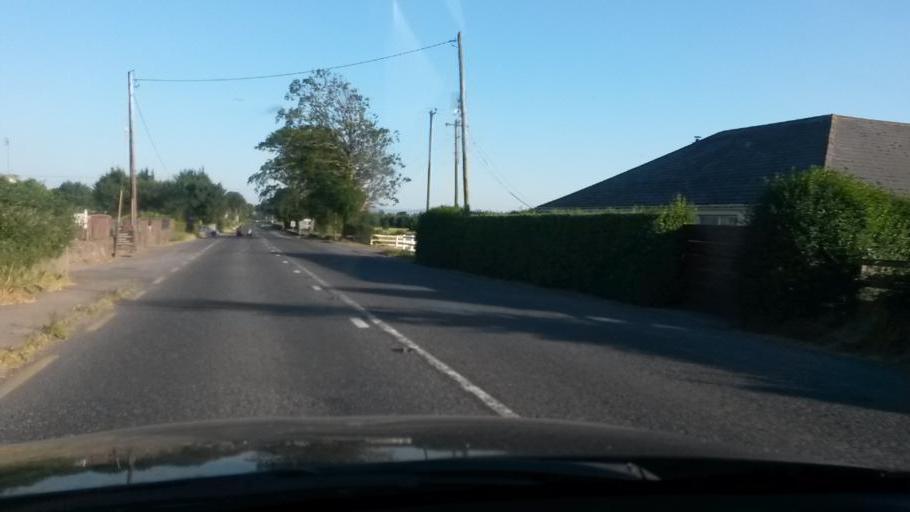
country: IE
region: Leinster
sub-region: Dublin City
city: Finglas
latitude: 53.4384
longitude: -6.3364
